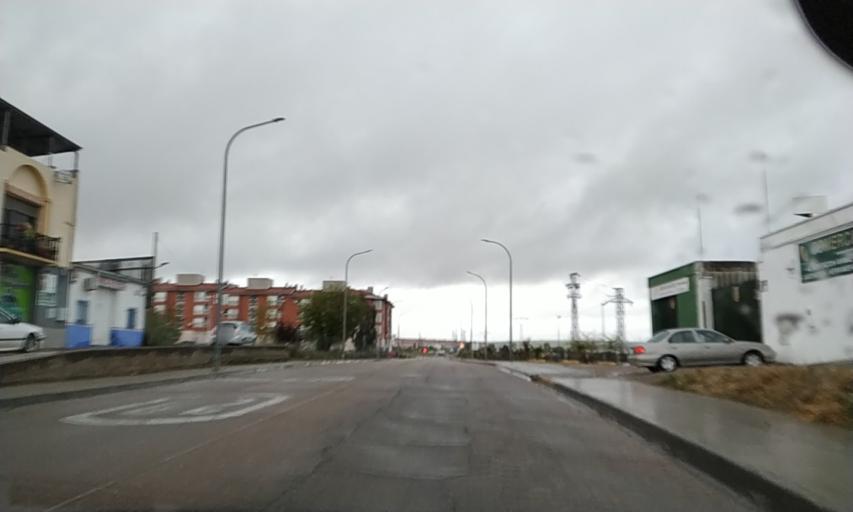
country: ES
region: Extremadura
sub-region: Provincia de Badajoz
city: Merida
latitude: 38.9272
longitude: -6.3376
